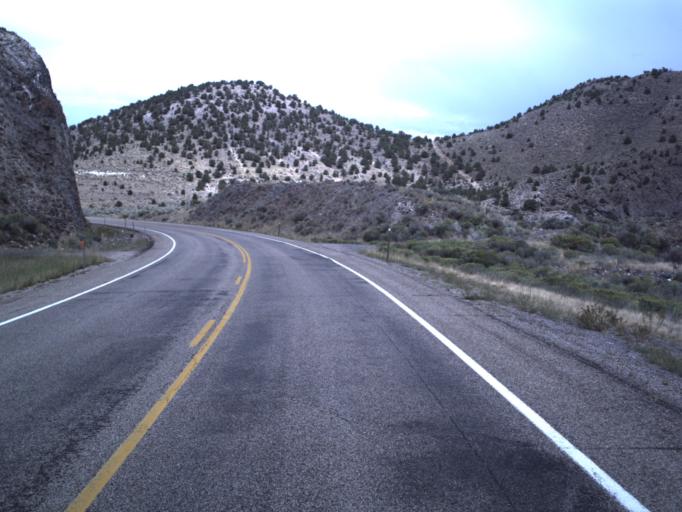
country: US
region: Utah
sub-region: Piute County
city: Junction
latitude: 38.1305
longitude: -112.3179
